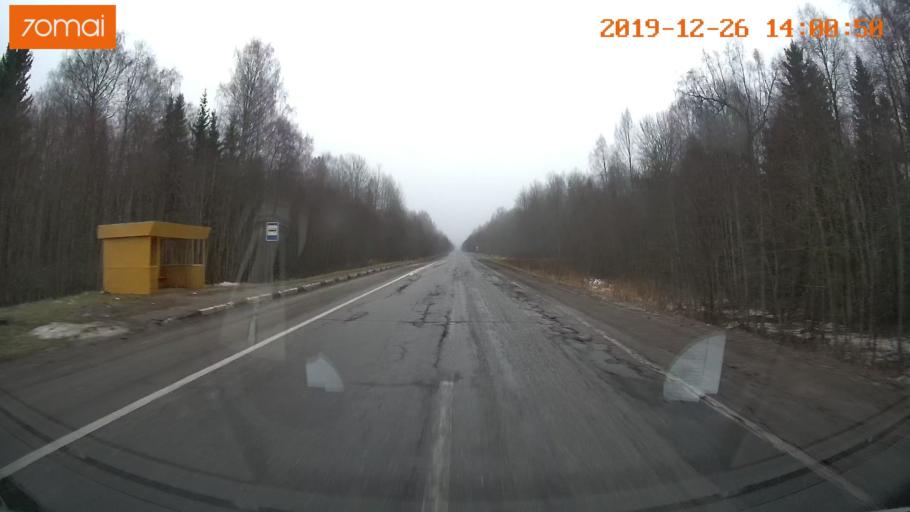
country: RU
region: Jaroslavl
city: Poshekhon'ye
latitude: 58.5552
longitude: 38.7514
